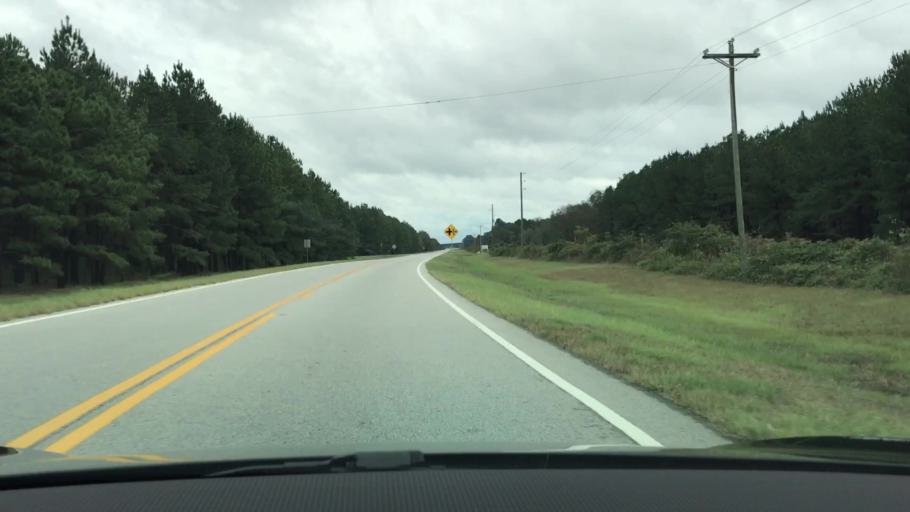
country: US
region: Georgia
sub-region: Glascock County
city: Gibson
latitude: 33.3045
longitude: -82.5239
